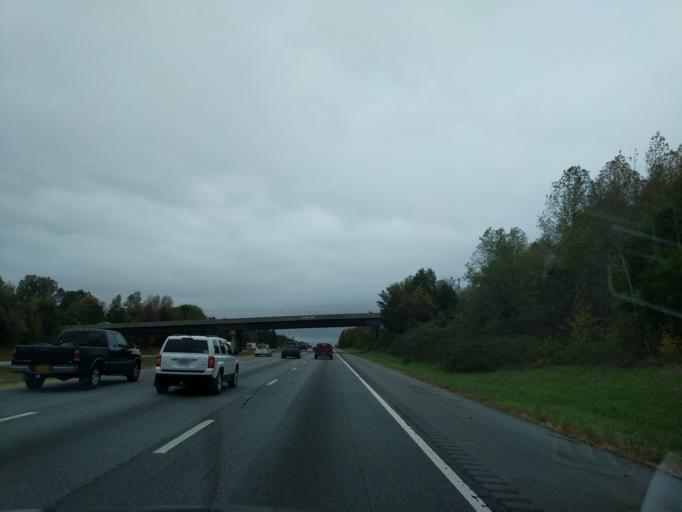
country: US
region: North Carolina
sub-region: Randolph County
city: Trinity
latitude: 35.8861
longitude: -79.9918
